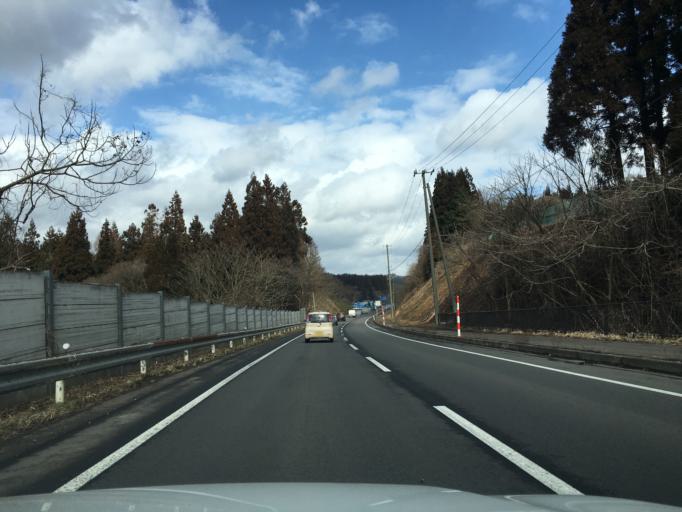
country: JP
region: Akita
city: Takanosu
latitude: 40.0273
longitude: 140.2738
